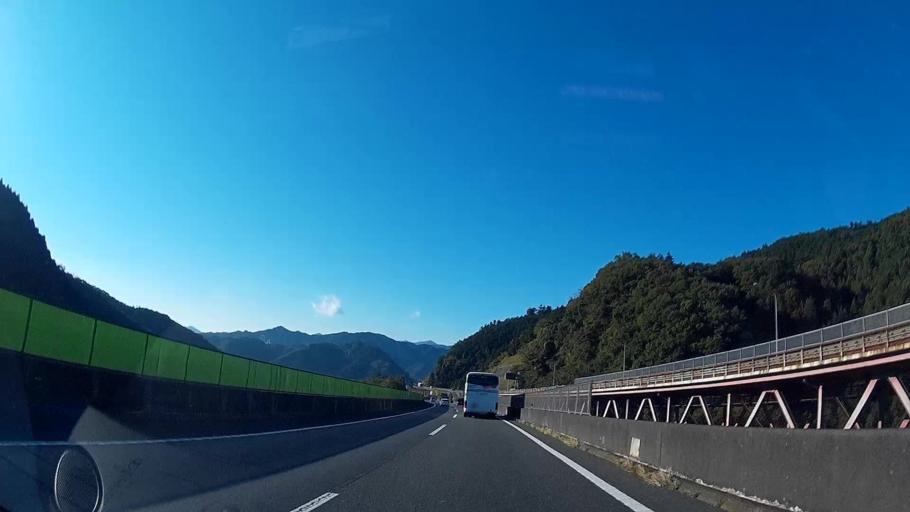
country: JP
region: Yamanashi
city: Uenohara
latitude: 35.6312
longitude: 139.2042
